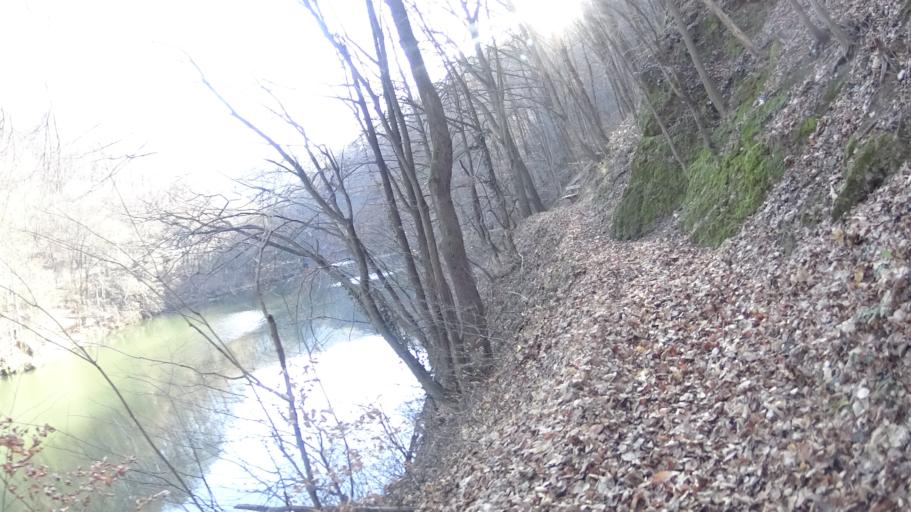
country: HU
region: Borsod-Abauj-Zemplen
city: Sajobabony
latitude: 48.1096
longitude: 20.6144
